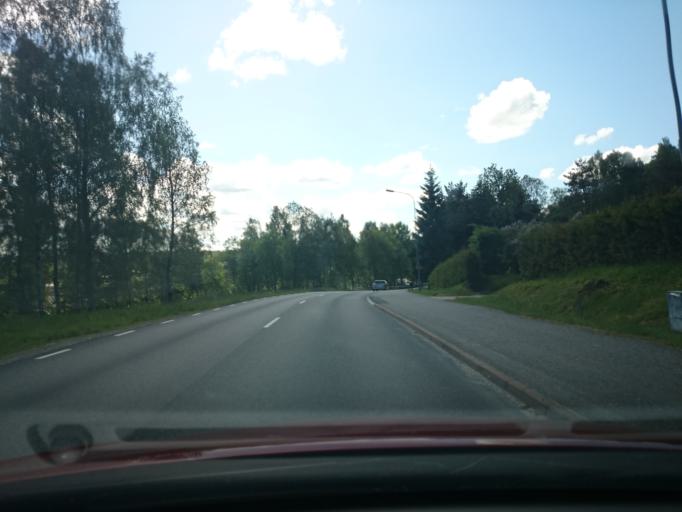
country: SE
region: Vaestra Goetaland
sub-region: Harryda Kommun
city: Landvetter
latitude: 57.6913
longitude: 12.2066
